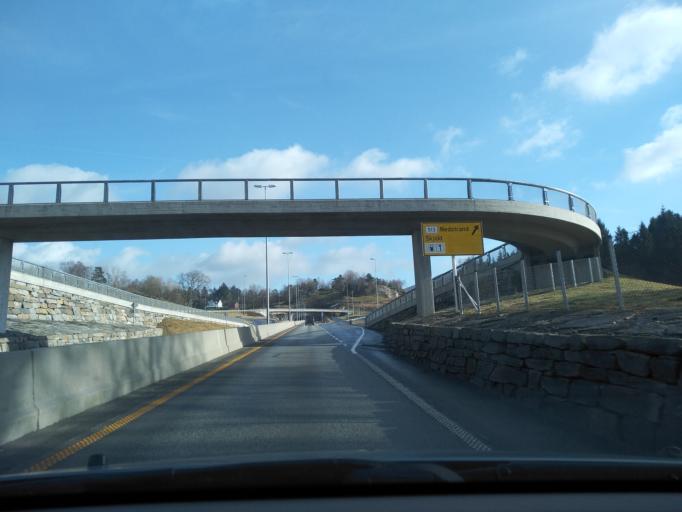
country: NO
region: Rogaland
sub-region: Tysvaer
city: Aksdal
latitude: 59.5062
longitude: 5.6062
